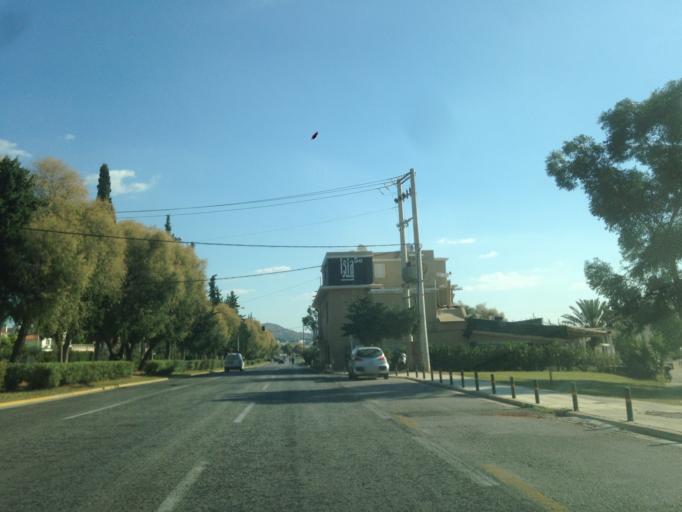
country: GR
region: Attica
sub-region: Nomarchia Anatolikis Attikis
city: Voula
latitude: 37.8408
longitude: 23.7601
